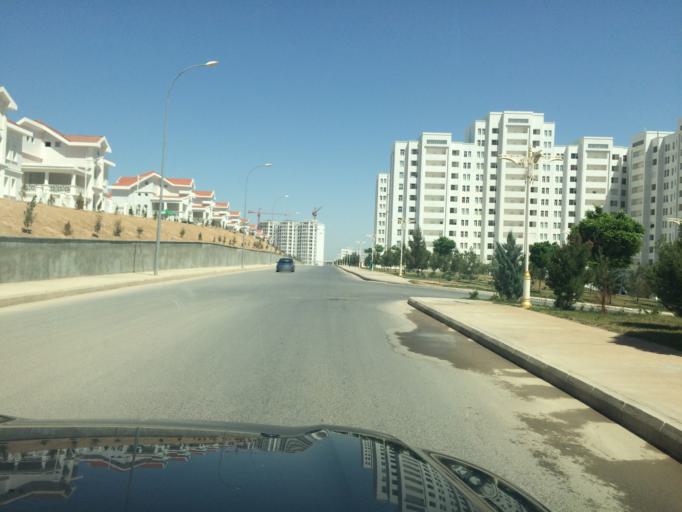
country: TM
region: Ahal
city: Ashgabat
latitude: 37.9327
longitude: 58.3650
